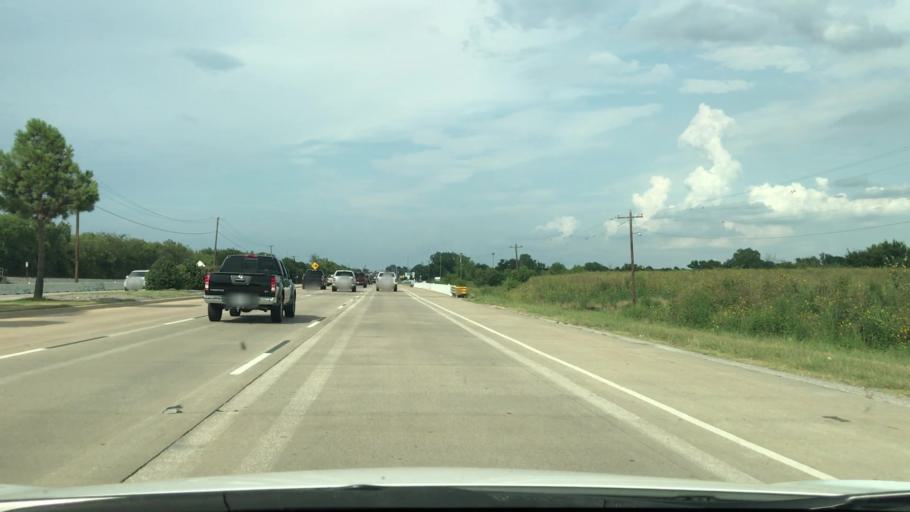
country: US
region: Texas
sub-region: Collin County
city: Wylie
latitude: 32.9949
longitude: -96.5660
